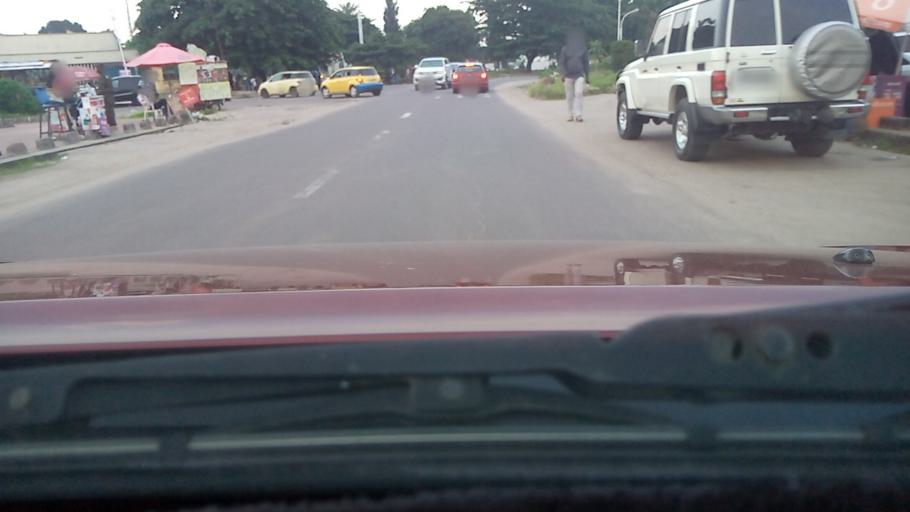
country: CD
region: Kinshasa
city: Kinshasa
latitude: -4.3065
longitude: 15.2866
